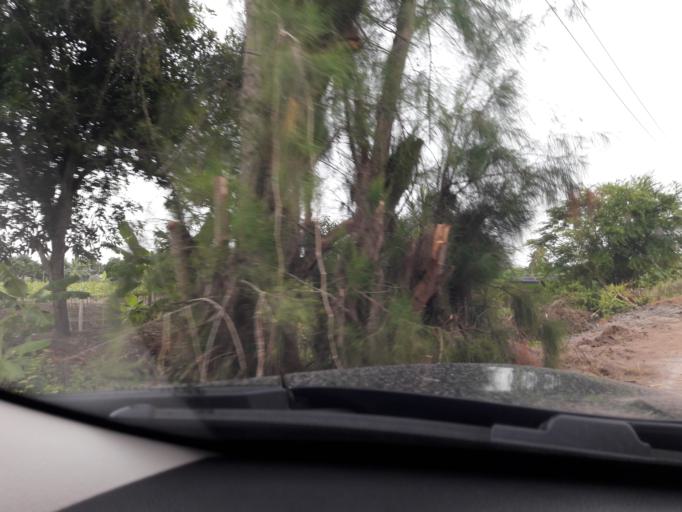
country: TH
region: Ratchaburi
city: Bang Phae
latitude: 13.6173
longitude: 99.9690
